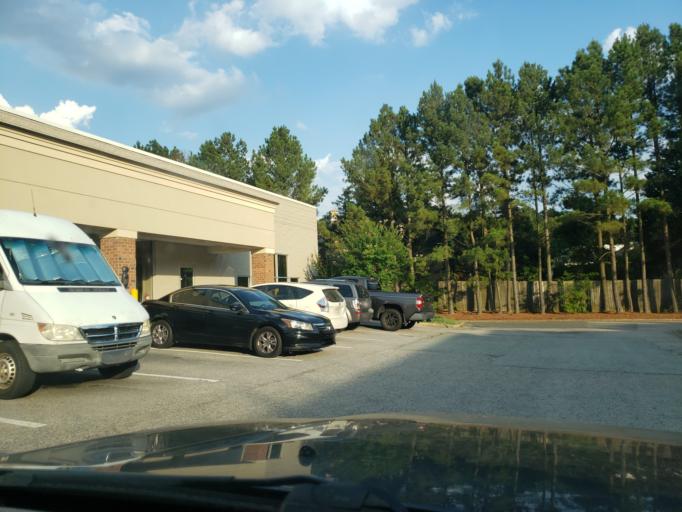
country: US
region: North Carolina
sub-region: Orange County
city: Chapel Hill
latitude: 35.9094
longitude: -78.9859
